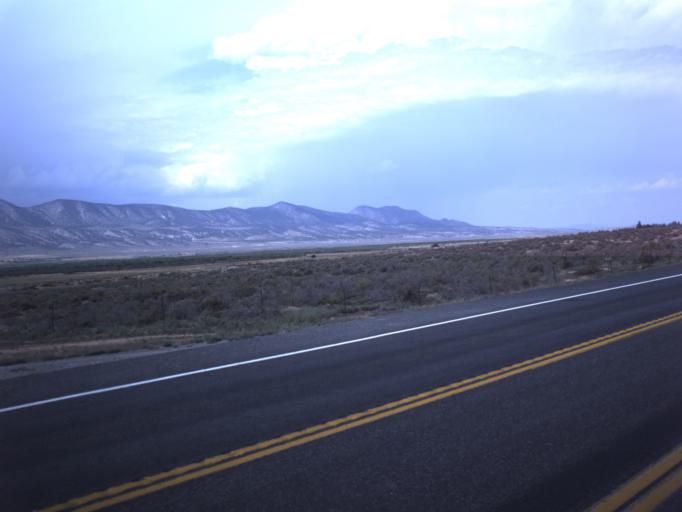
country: US
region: Utah
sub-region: Sanpete County
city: Gunnison
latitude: 39.2070
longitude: -111.8483
